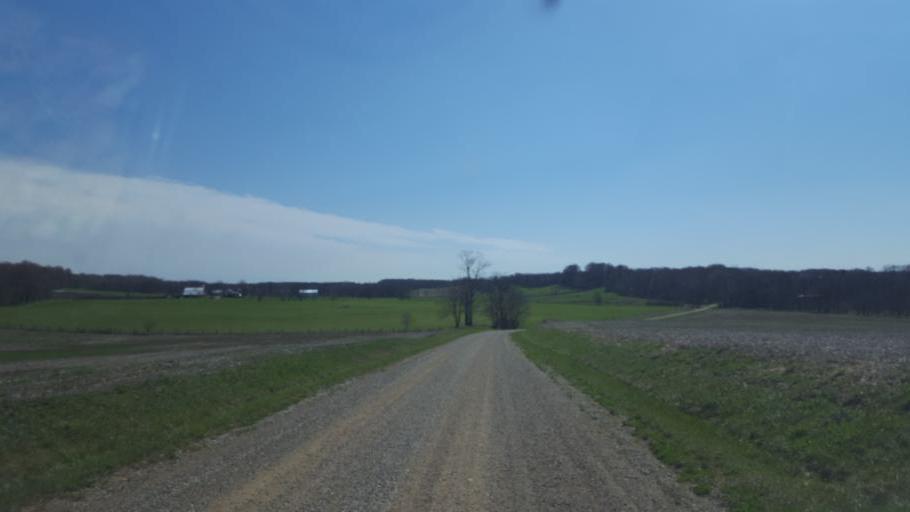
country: US
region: Ohio
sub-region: Knox County
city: Gambier
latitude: 40.3469
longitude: -82.3698
